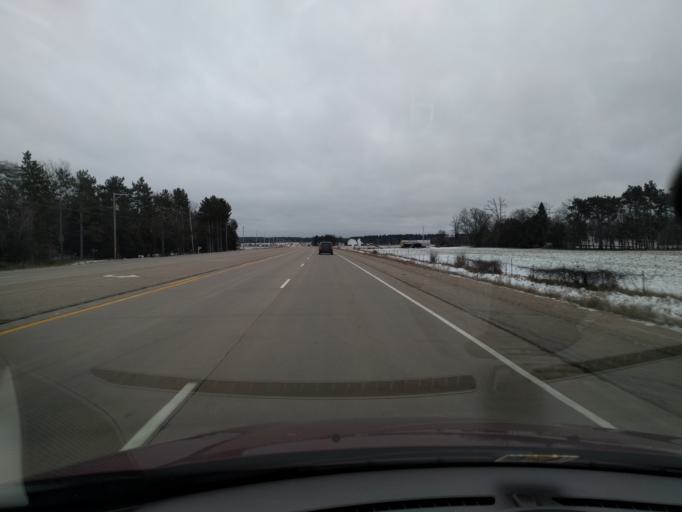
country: US
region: Wisconsin
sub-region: Portage County
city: Whiting
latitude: 44.5222
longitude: -89.4698
